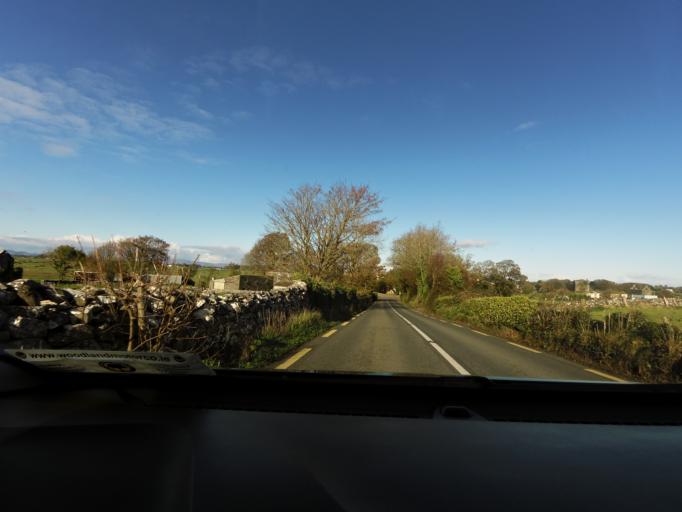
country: IE
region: Connaught
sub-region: Maigh Eo
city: Ballinrobe
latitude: 53.5155
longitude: -9.0850
